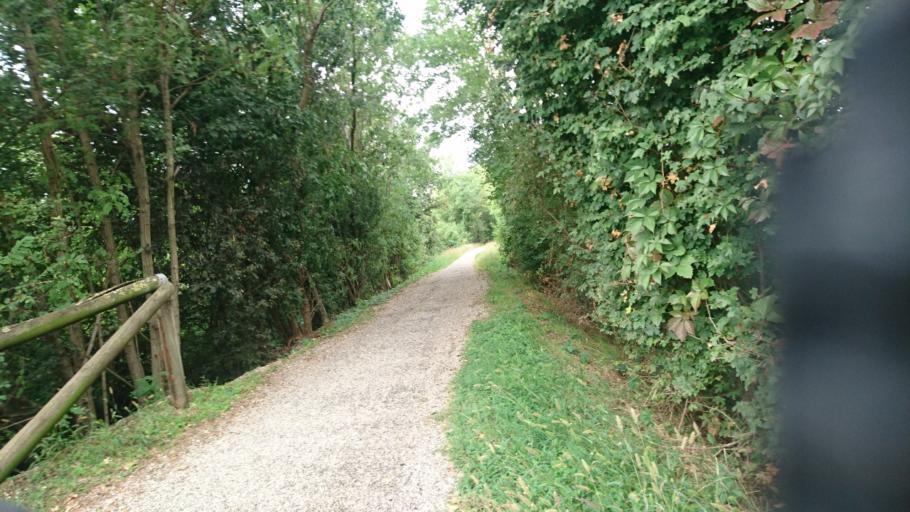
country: IT
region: Veneto
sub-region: Provincia di Vicenza
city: Montebello Vicentino
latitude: 45.4696
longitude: 11.3868
